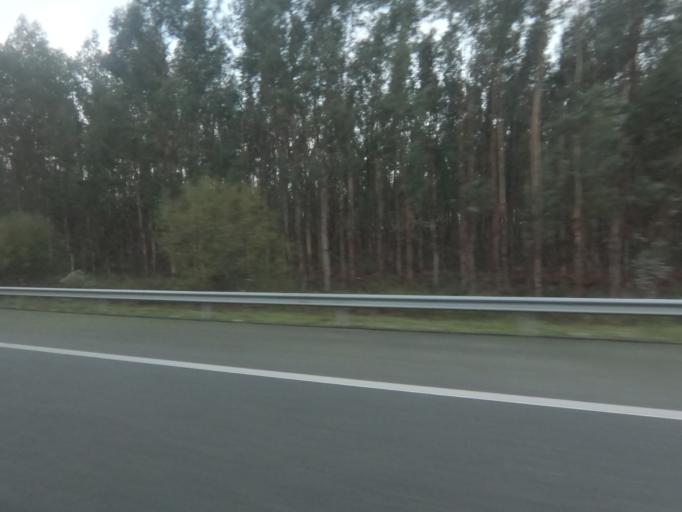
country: PT
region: Braga
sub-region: Barcelos
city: Galegos
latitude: 41.6290
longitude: -8.5610
